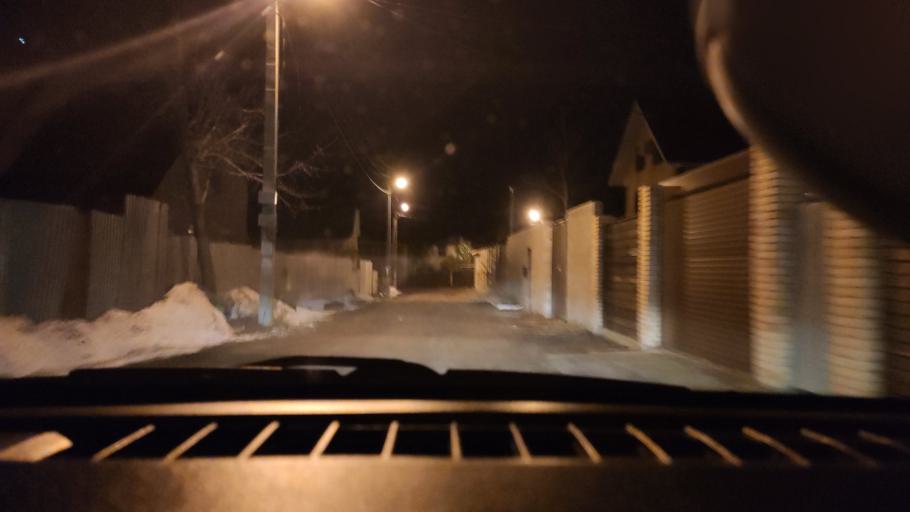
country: RU
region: Samara
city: Samara
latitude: 53.2683
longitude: 50.2316
